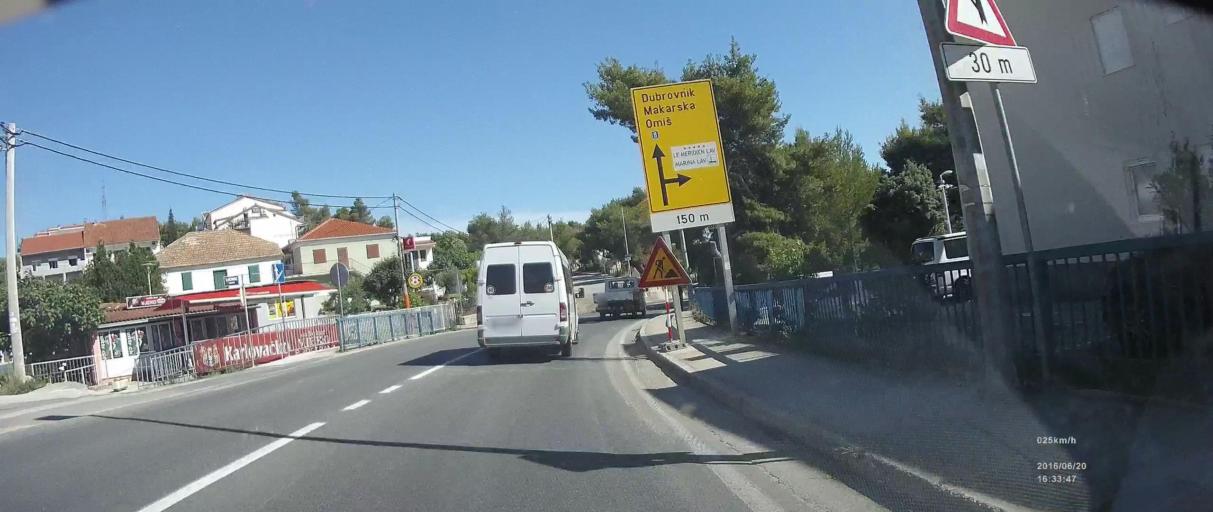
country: HR
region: Splitsko-Dalmatinska
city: Podstrana
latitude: 43.4951
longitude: 16.5385
